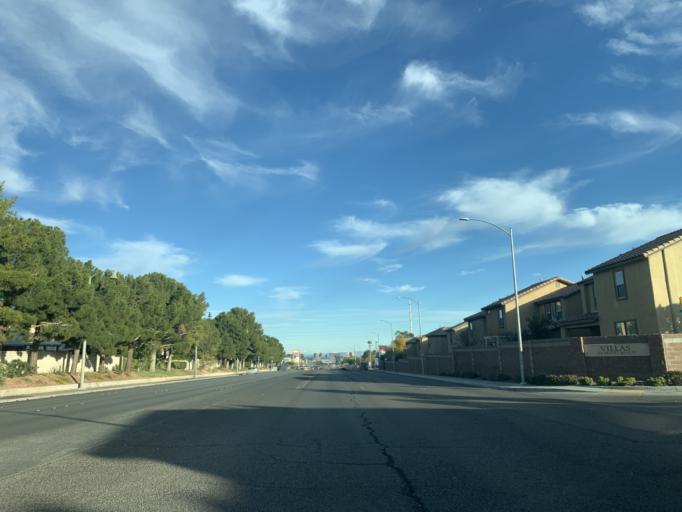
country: US
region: Nevada
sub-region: Clark County
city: Spring Valley
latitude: 36.1295
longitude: -115.2817
